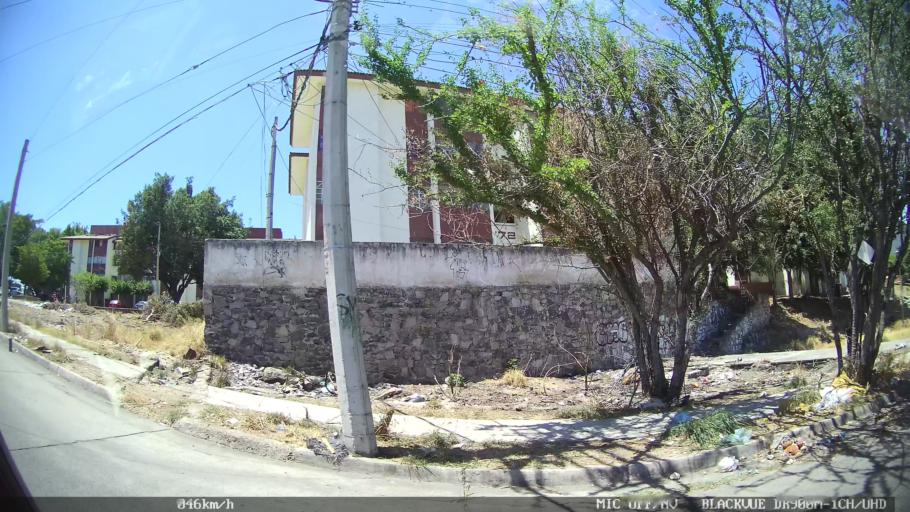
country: MX
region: Jalisco
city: Tlaquepaque
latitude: 20.6860
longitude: -103.2819
